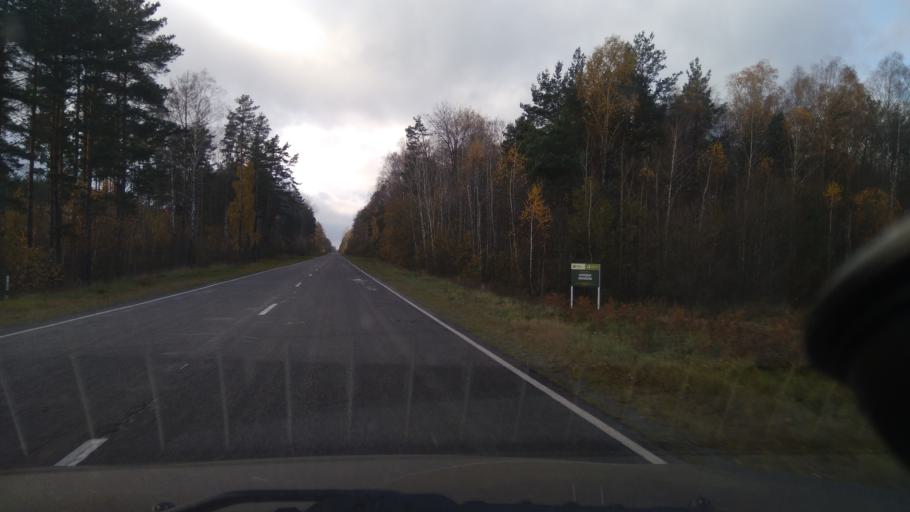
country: BY
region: Minsk
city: Urechcha
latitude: 53.2095
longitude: 27.9768
